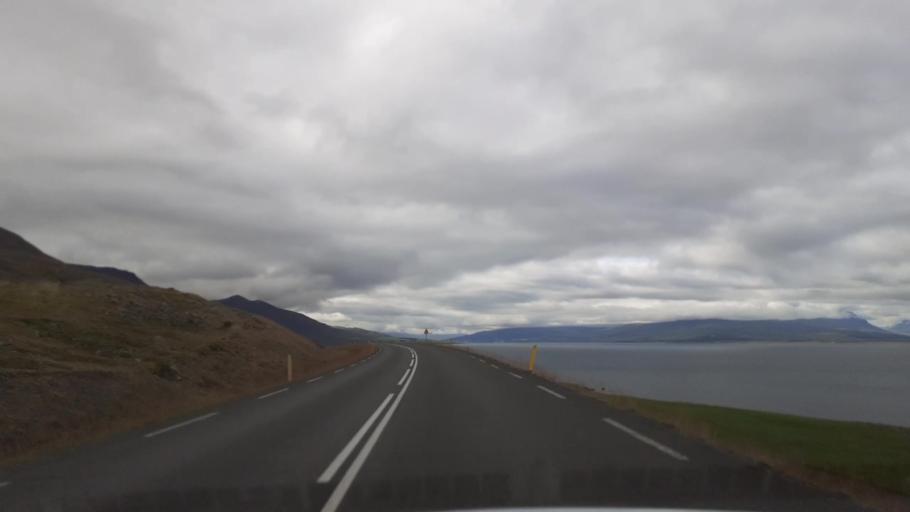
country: IS
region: Northeast
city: Akureyri
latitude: 65.8736
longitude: -18.0771
